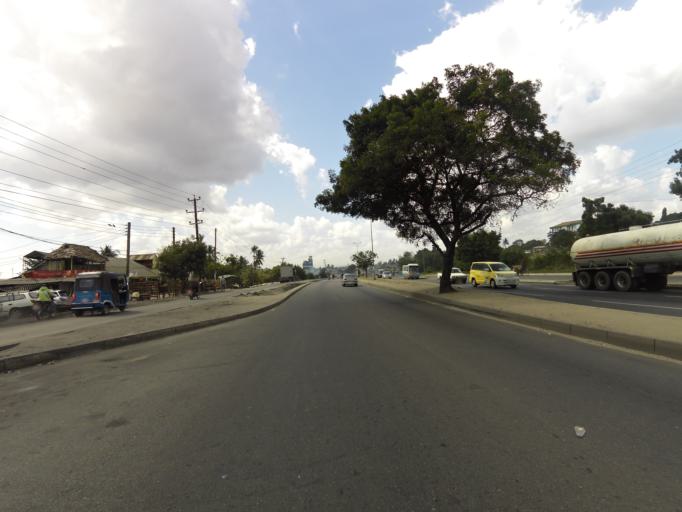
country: TZ
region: Dar es Salaam
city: Magomeni
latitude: -6.8062
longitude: 39.2138
